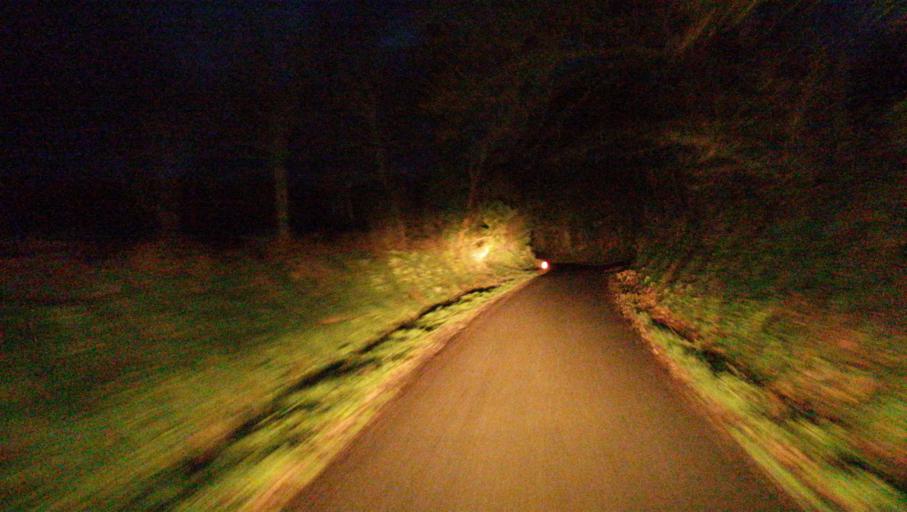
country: FR
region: Brittany
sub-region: Departement des Cotes-d'Armor
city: Plehedel
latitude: 48.6864
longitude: -3.0335
